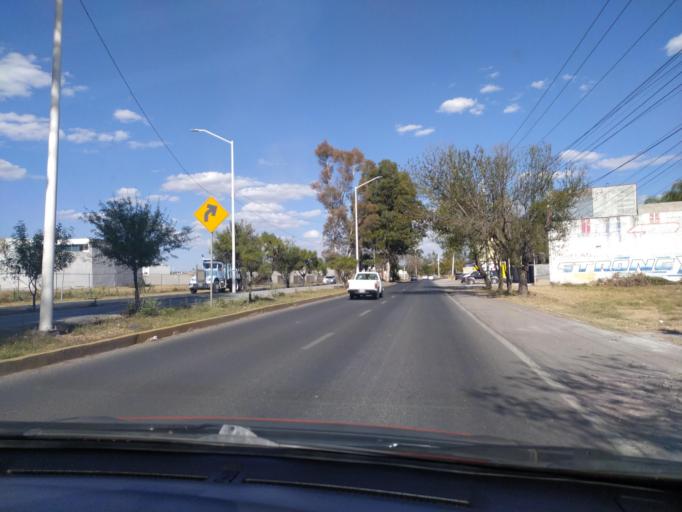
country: LA
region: Oudomxai
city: Muang La
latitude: 21.0307
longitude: 101.8432
